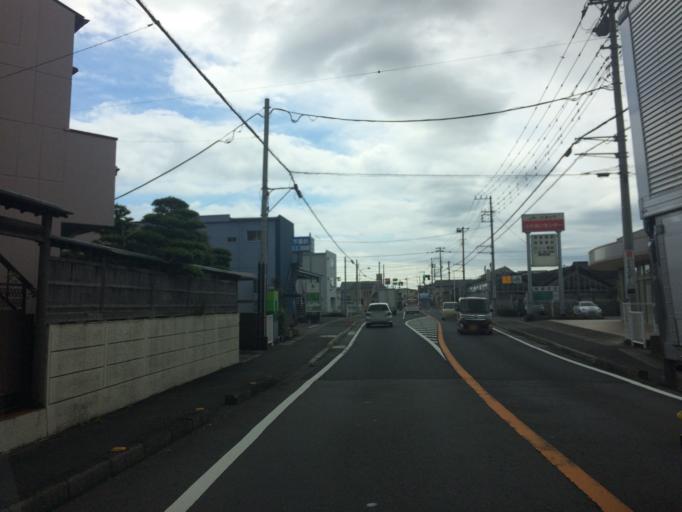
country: JP
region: Shizuoka
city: Fuji
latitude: 35.1675
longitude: 138.6490
